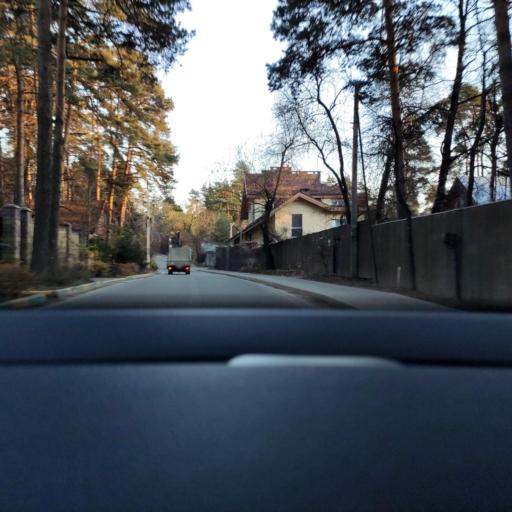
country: RU
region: Moscow
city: Zagor'ye
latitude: 55.5441
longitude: 37.6767
